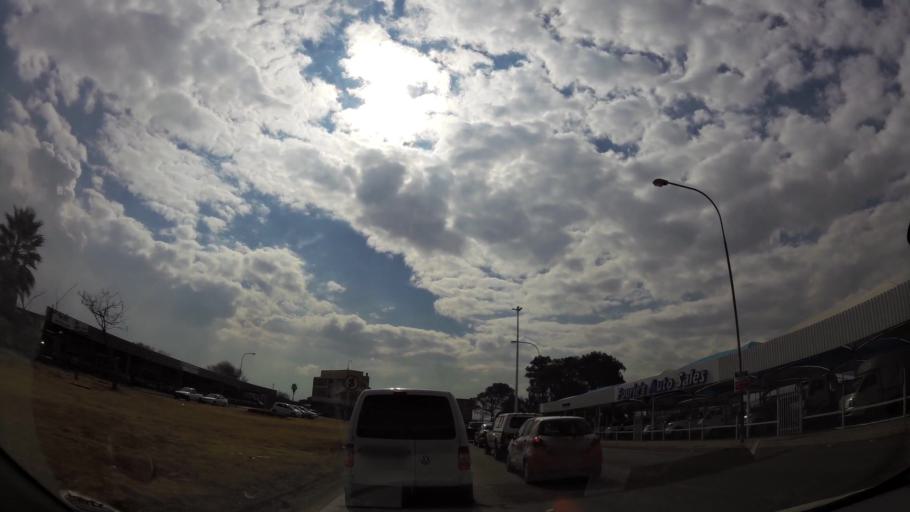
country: ZA
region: Gauteng
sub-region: Sedibeng District Municipality
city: Vereeniging
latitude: -26.6653
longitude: 27.9205
